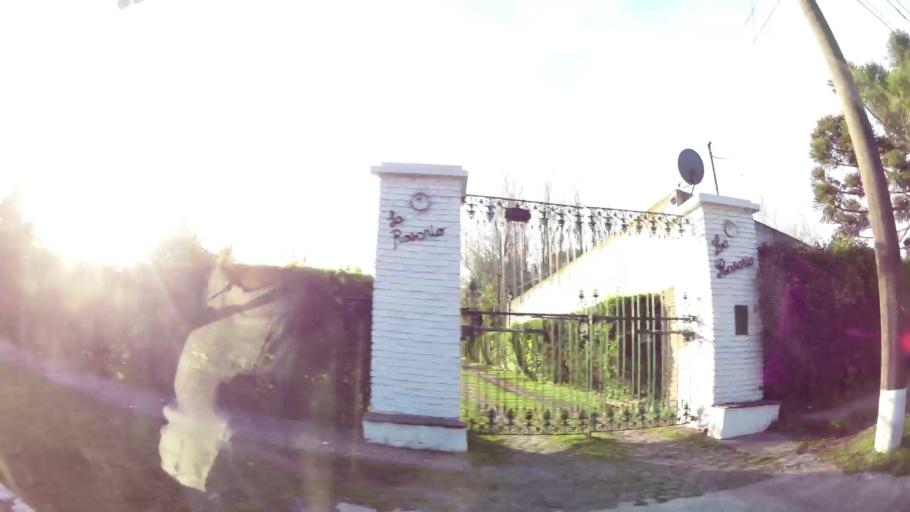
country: AR
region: Buenos Aires
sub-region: Partido de Quilmes
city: Quilmes
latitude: -34.8064
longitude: -58.2071
